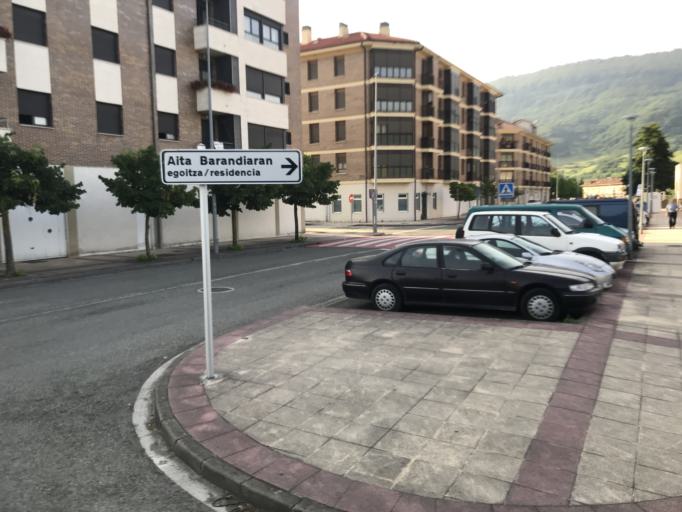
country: ES
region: Navarre
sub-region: Provincia de Navarra
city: Altsasu
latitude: 42.8949
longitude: -2.1757
